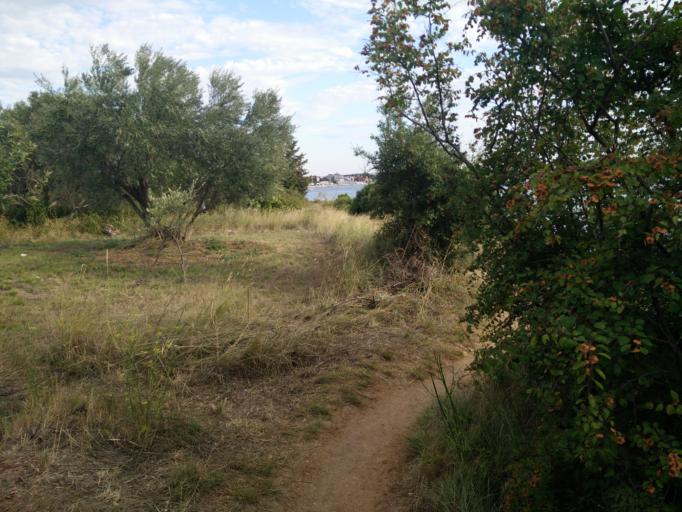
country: HR
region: Zadarska
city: Biograd na Moru
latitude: 43.9507
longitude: 15.4402
